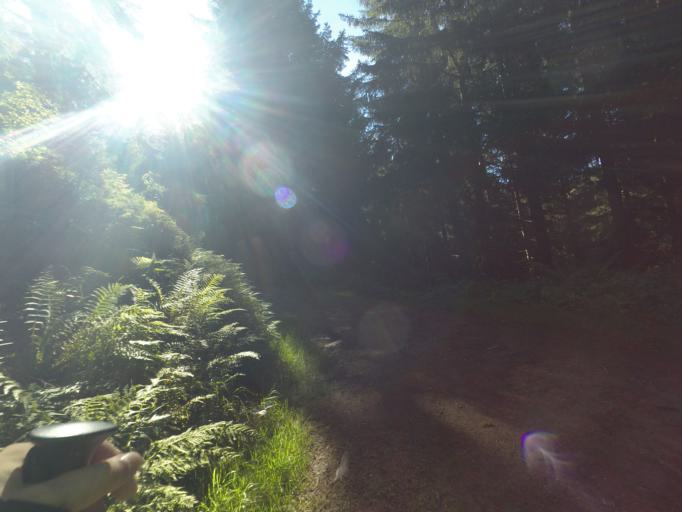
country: AT
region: Salzburg
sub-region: Politischer Bezirk Salzburg-Umgebung
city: Hintersee
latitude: 47.6967
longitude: 13.2521
